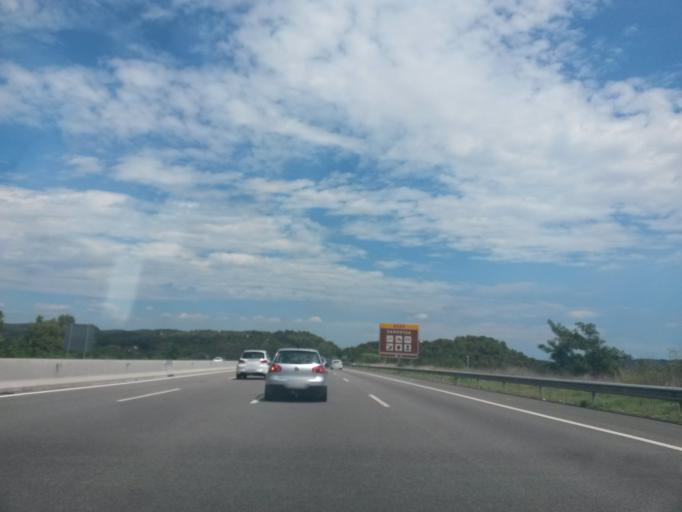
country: ES
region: Catalonia
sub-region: Provincia de Girona
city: Sarria de Ter
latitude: 42.0055
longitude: 2.8073
